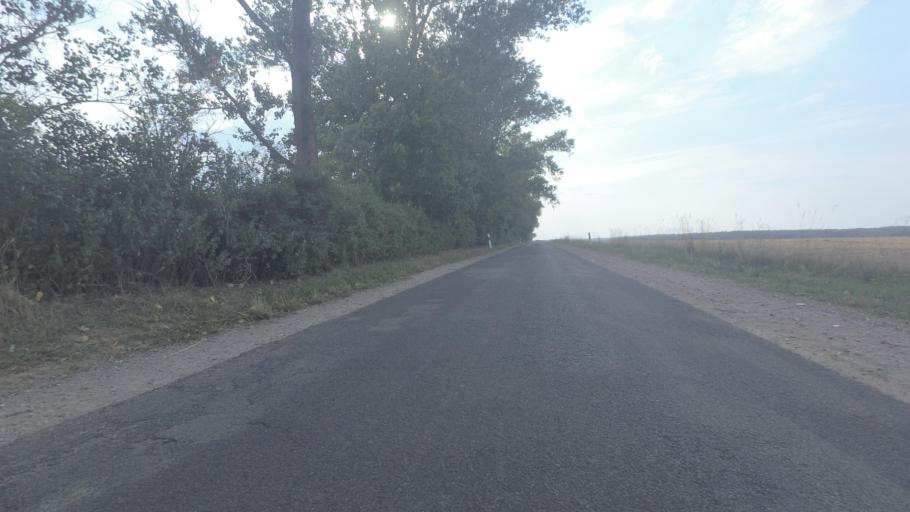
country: DE
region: Brandenburg
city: Heiligengrabe
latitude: 53.2436
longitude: 12.3993
